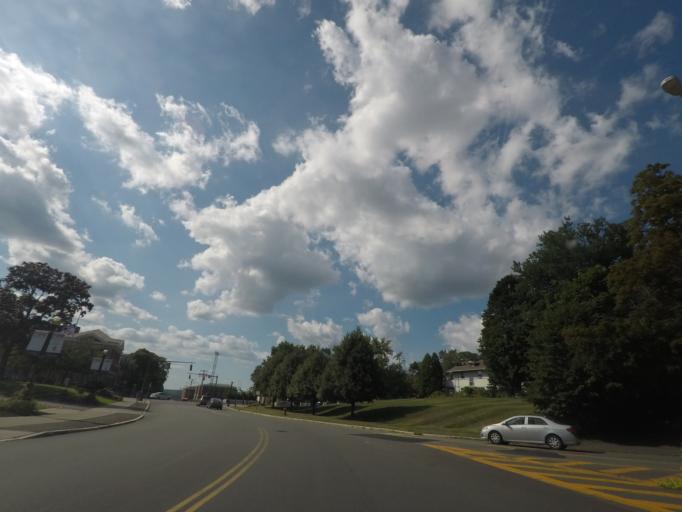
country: US
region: New York
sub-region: Rensselaer County
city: Troy
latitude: 42.7305
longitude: -73.6762
